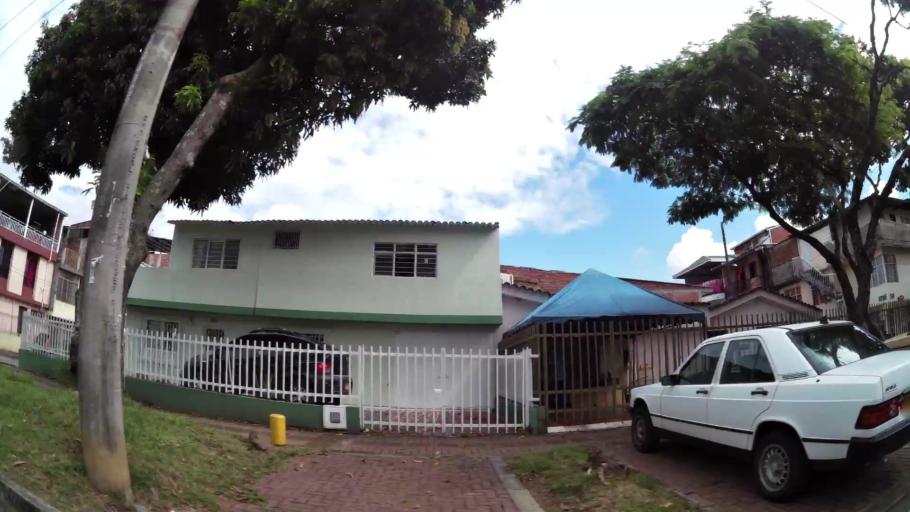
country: CO
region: Valle del Cauca
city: Cali
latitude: 3.3859
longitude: -76.5492
